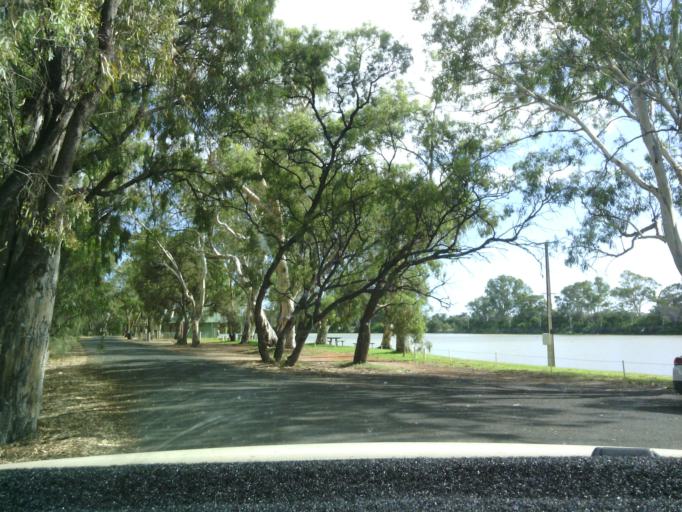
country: AU
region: South Australia
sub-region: Berri and Barmera
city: Berri
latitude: -34.2875
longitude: 140.6317
